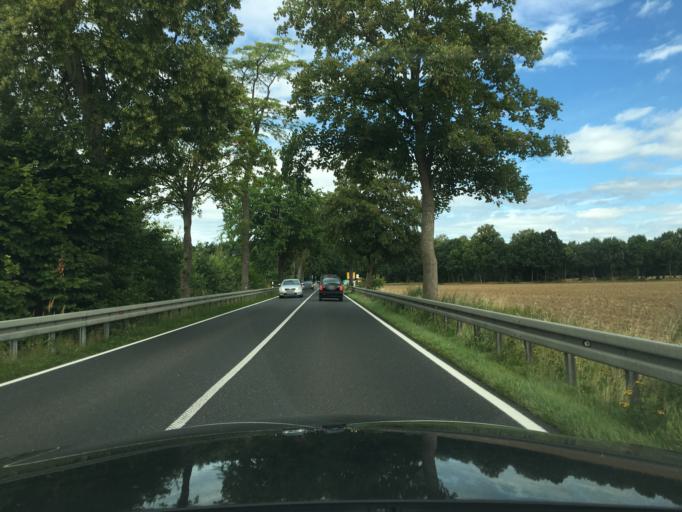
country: DE
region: Brandenburg
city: Gransee
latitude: 52.9636
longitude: 13.1490
